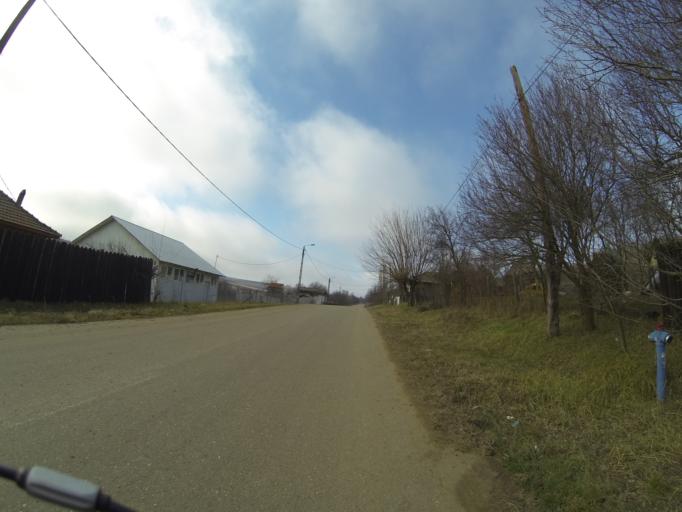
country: RO
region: Mehedinti
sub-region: Comuna Poroina Mare
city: Poroina Mare
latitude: 44.4945
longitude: 22.9939
